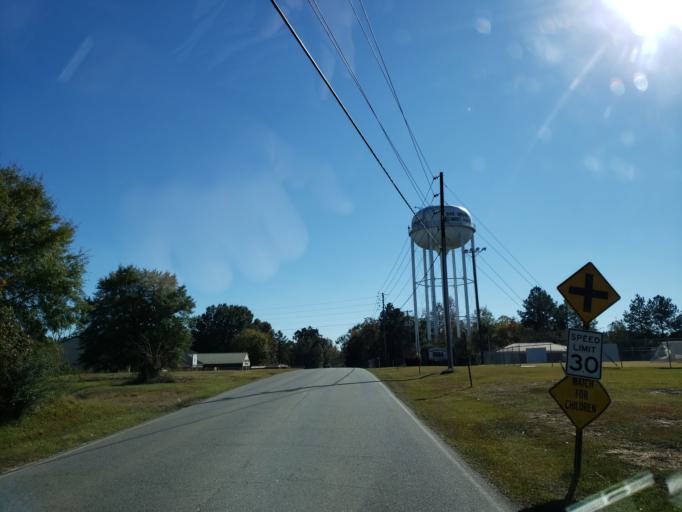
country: US
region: Mississippi
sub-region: Lamar County
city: West Hattiesburg
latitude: 31.3165
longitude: -89.3992
